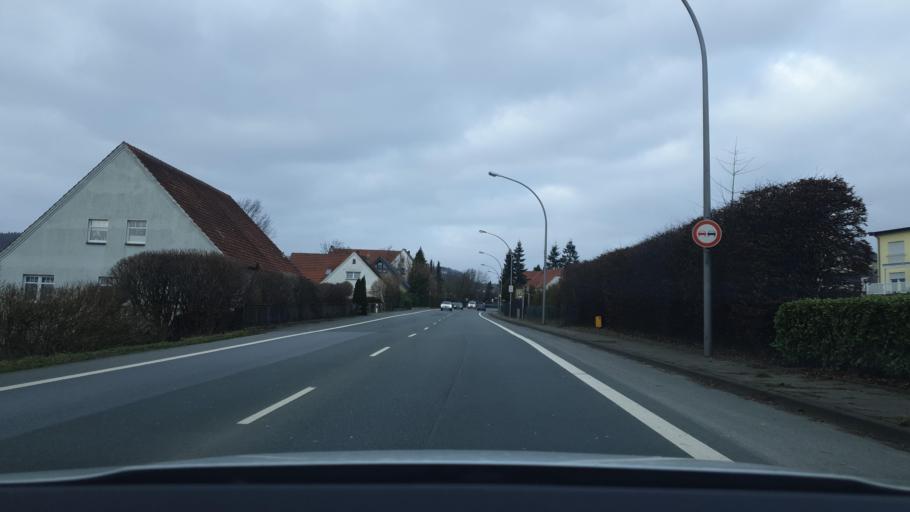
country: DE
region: North Rhine-Westphalia
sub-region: Regierungsbezirk Detmold
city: Huellhorst
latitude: 52.2649
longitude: 8.6358
